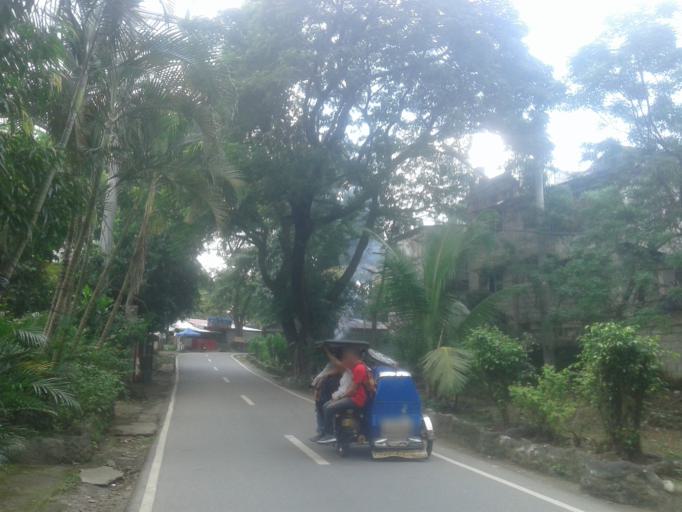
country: PH
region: Metro Manila
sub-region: Mandaluyong
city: Mandaluyong City
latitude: 14.5836
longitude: 121.0400
